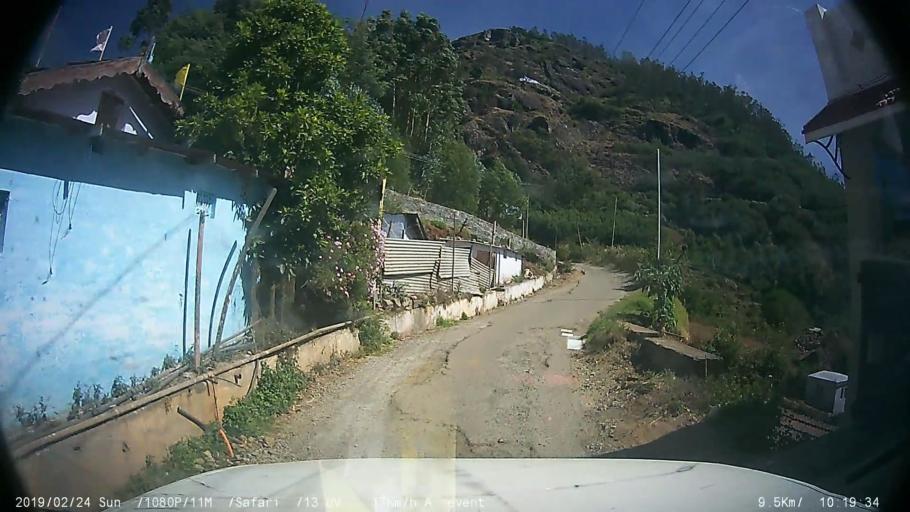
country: IN
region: Tamil Nadu
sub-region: Nilgiri
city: Ooty
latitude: 11.3870
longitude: 76.7198
